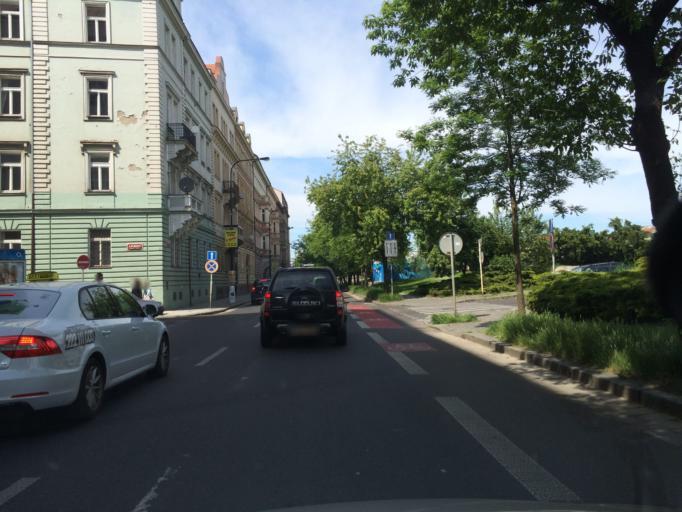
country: CZ
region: Praha
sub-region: Praha 2
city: Vysehrad
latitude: 50.0705
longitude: 14.4105
